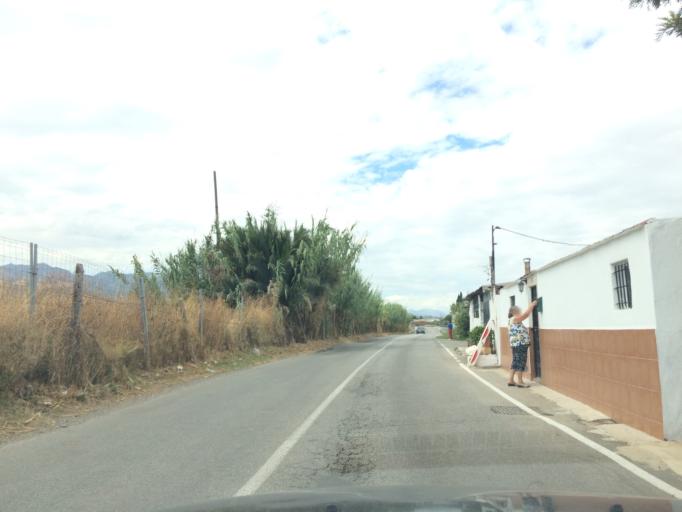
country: ES
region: Andalusia
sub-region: Provincia de Malaga
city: Alhaurin de la Torre
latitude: 36.6877
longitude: -4.5243
